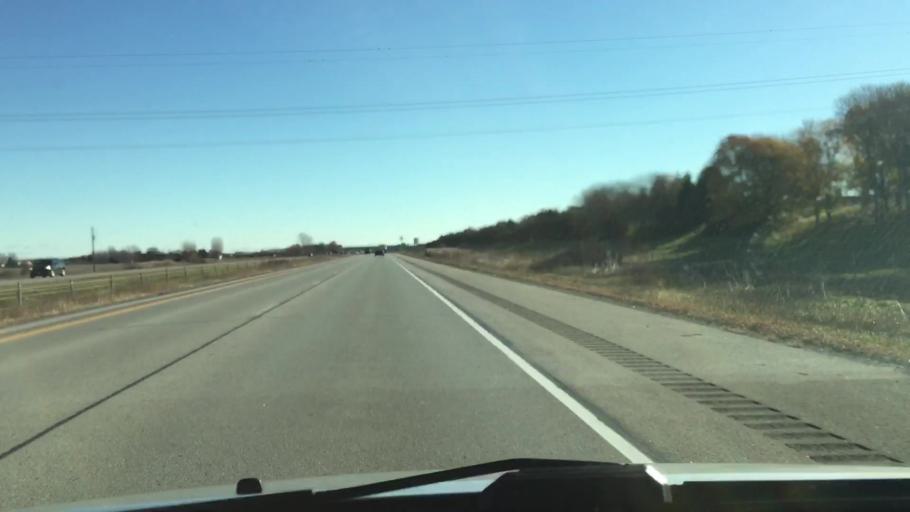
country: US
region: Wisconsin
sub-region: Outagamie County
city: Kimberly
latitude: 44.2978
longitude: -88.3447
